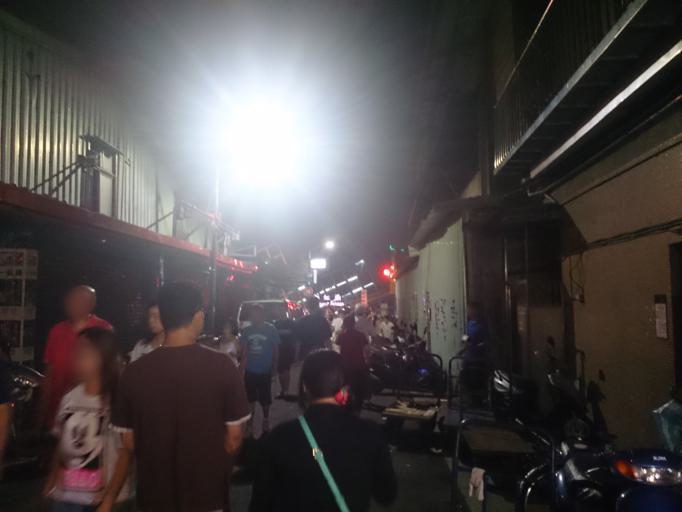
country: TW
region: Taipei
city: Taipei
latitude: 25.0510
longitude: 121.5766
